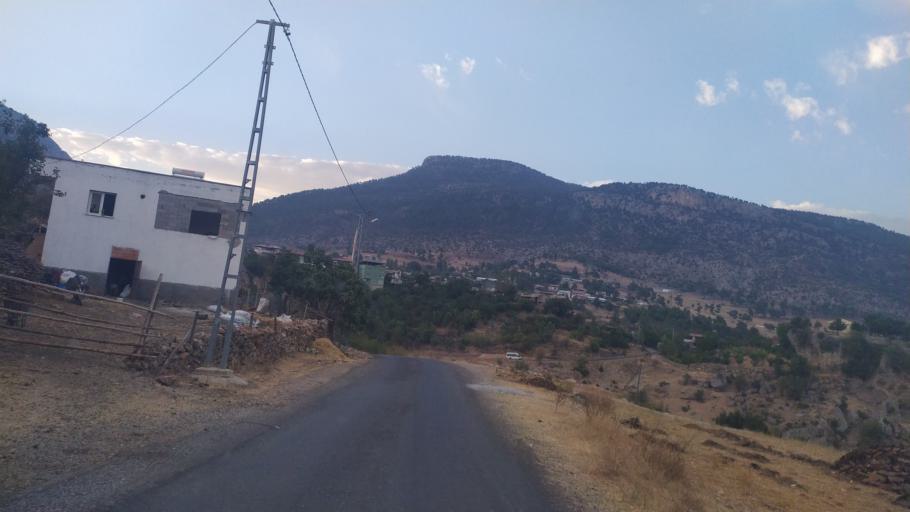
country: TR
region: Mersin
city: Camliyayla
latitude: 37.2361
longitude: 34.7179
